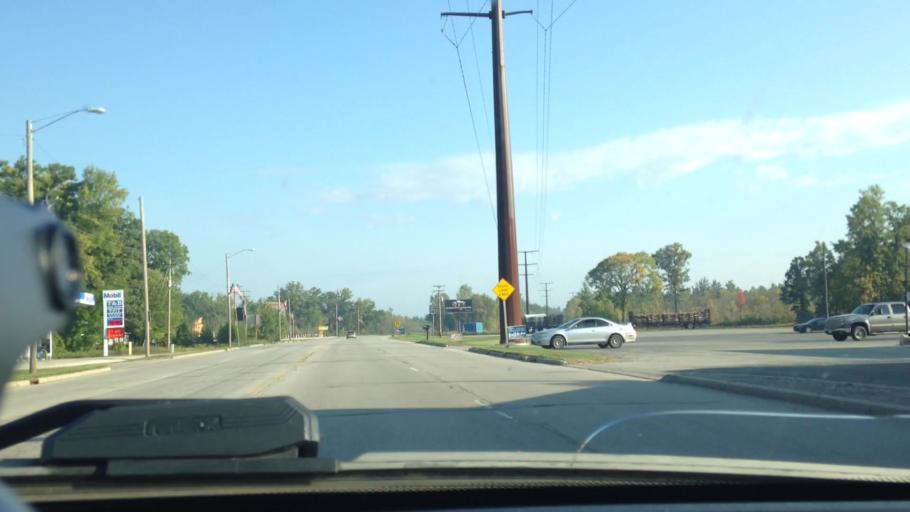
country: US
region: Wisconsin
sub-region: Marinette County
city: Peshtigo
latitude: 45.2332
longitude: -87.9964
